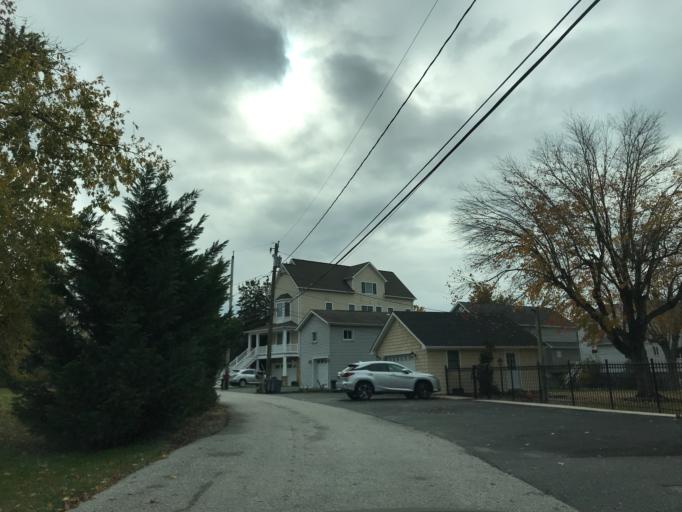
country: US
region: Maryland
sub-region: Baltimore County
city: Bowleys Quarters
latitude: 39.3215
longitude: -76.3998
